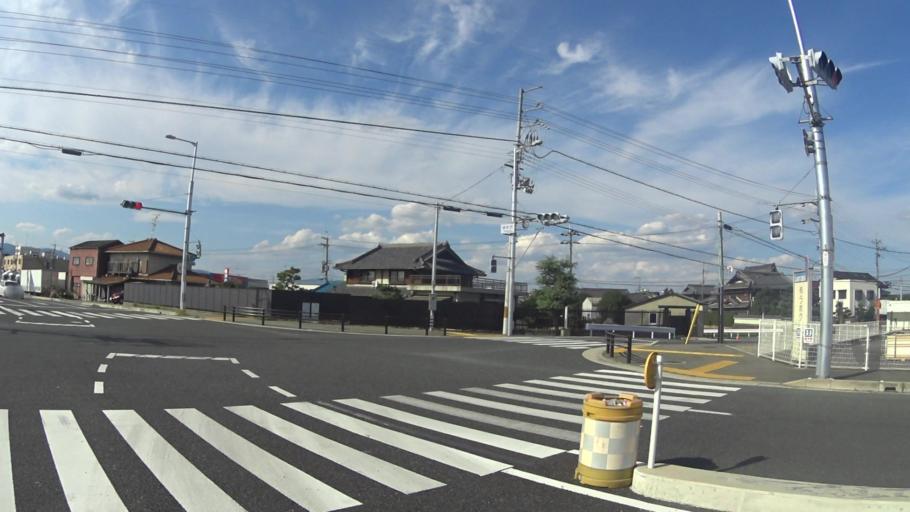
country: JP
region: Kyoto
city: Yawata
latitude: 34.8673
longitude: 135.7300
